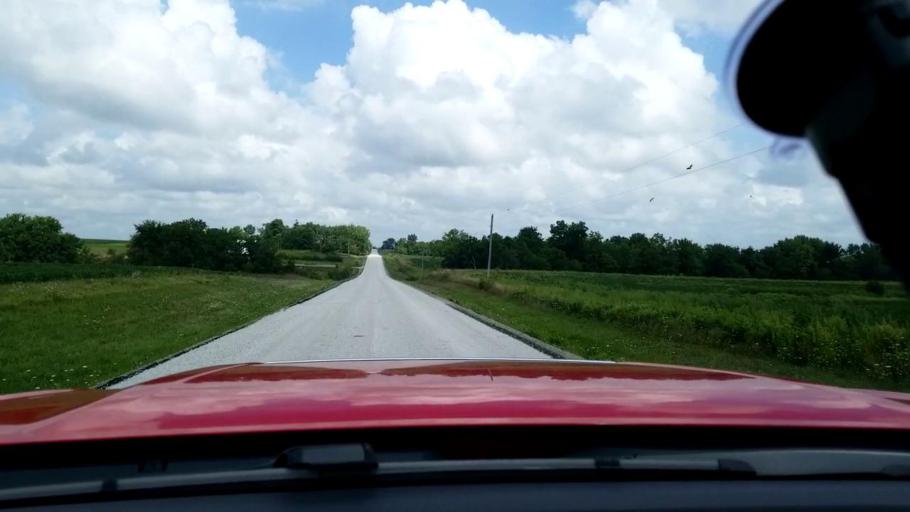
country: US
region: Iowa
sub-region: Decatur County
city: Lamoni
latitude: 40.6300
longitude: -94.0533
